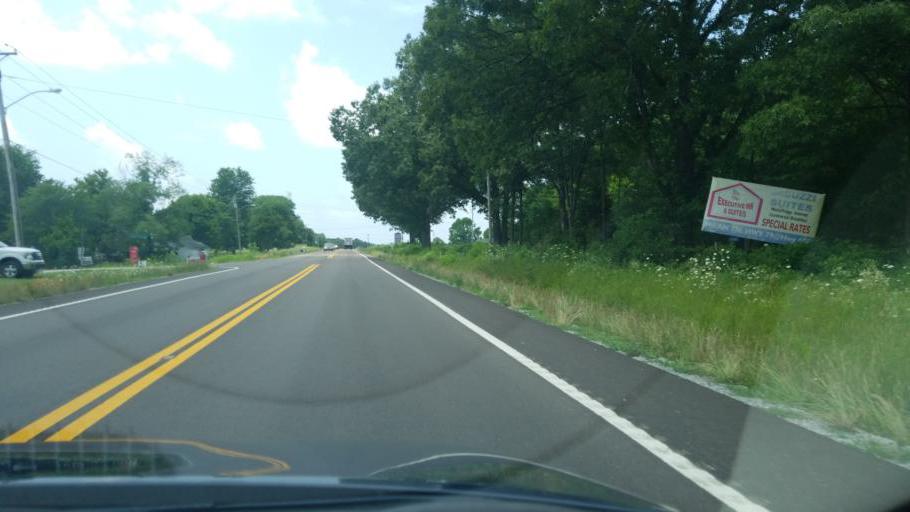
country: US
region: Tennessee
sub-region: Carroll County
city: Huntingdon
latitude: 36.0199
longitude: -88.3740
